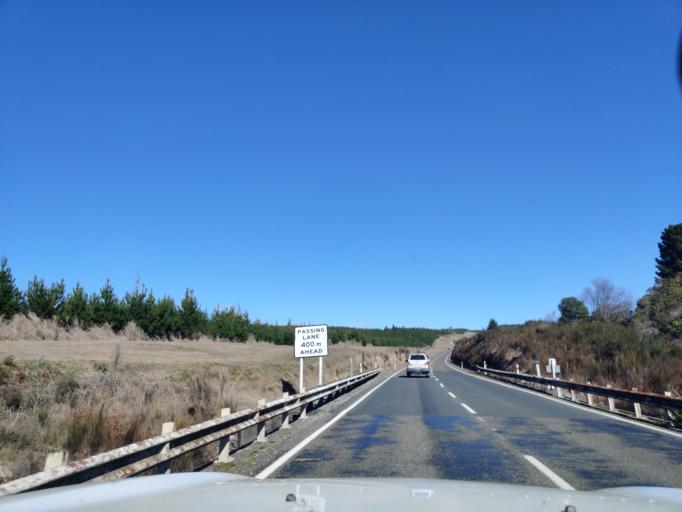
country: NZ
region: Waikato
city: Turangi
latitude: -39.1099
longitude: 175.8066
